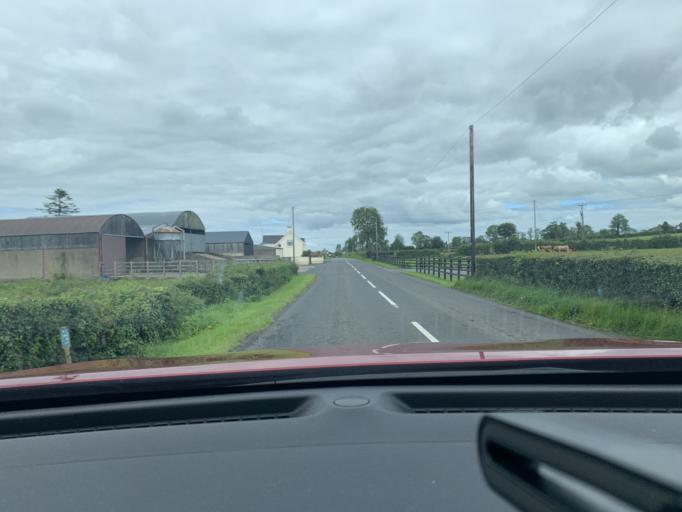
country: GB
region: Northern Ireland
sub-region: Fermanagh District
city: Enniskillen
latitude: 54.2753
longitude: -7.7033
